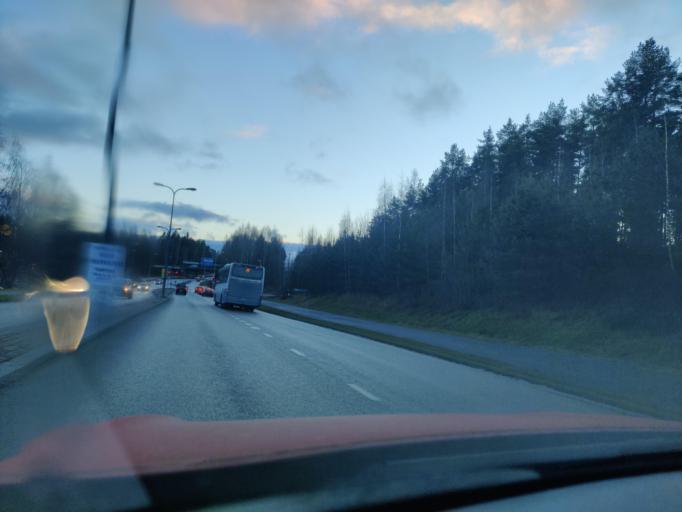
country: FI
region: Pirkanmaa
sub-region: Tampere
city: Nokia
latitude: 61.4668
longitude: 23.5044
